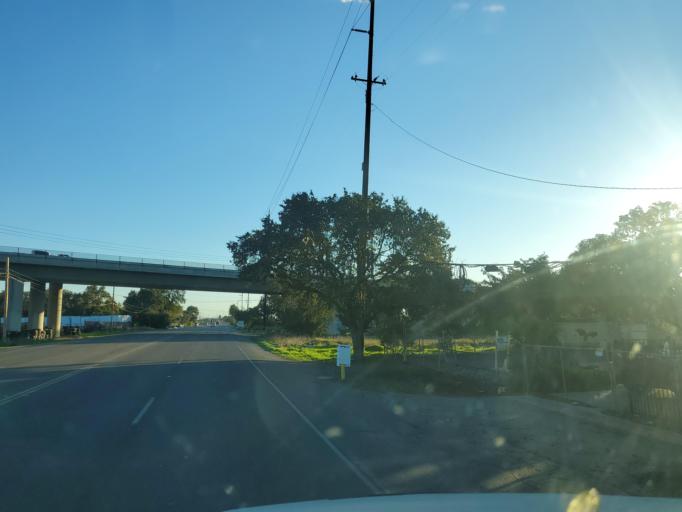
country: US
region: California
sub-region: San Joaquin County
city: French Camp
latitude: 37.8961
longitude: -121.2759
